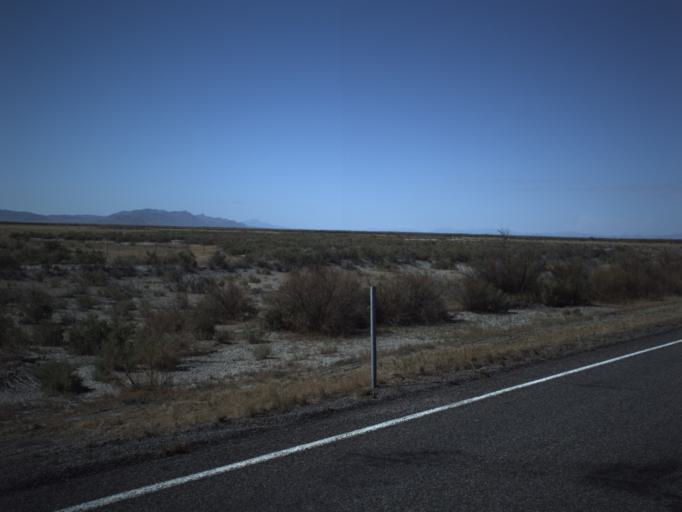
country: US
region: Utah
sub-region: Millard County
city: Delta
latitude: 39.3048
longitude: -112.8025
